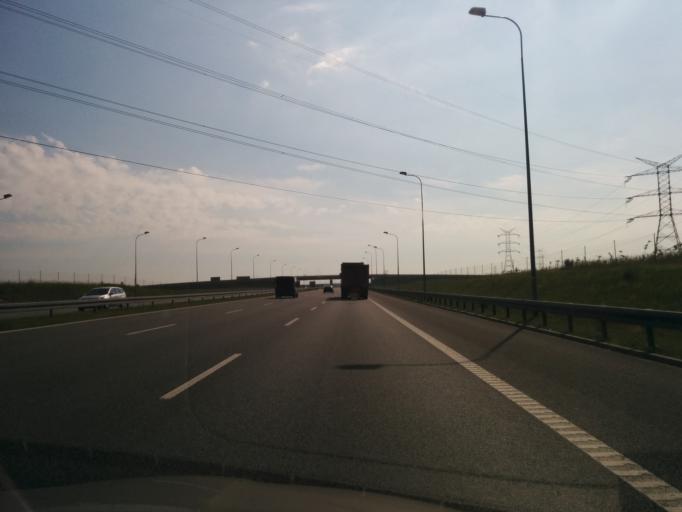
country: PL
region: Silesian Voivodeship
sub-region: Powiat tarnogorski
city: Wieszowa
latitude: 50.3722
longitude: 18.7514
